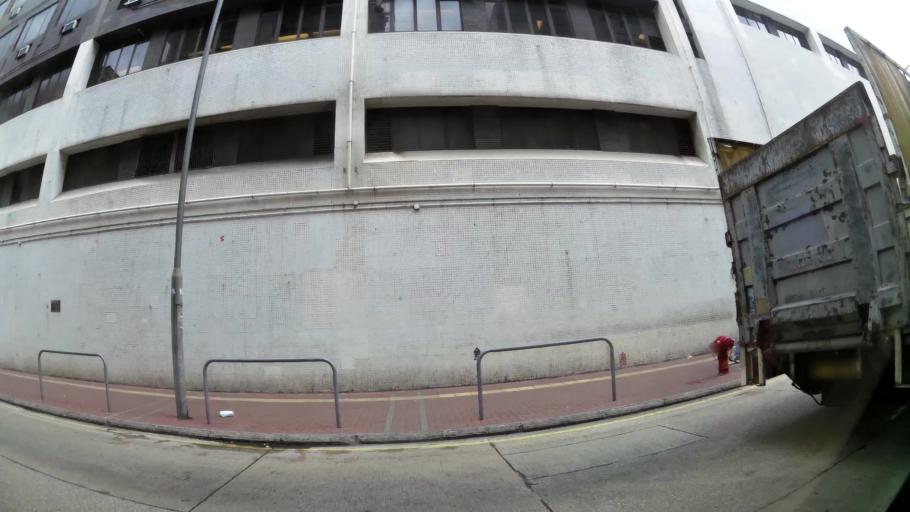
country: HK
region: Kowloon City
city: Kowloon
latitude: 22.3206
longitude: 114.1928
